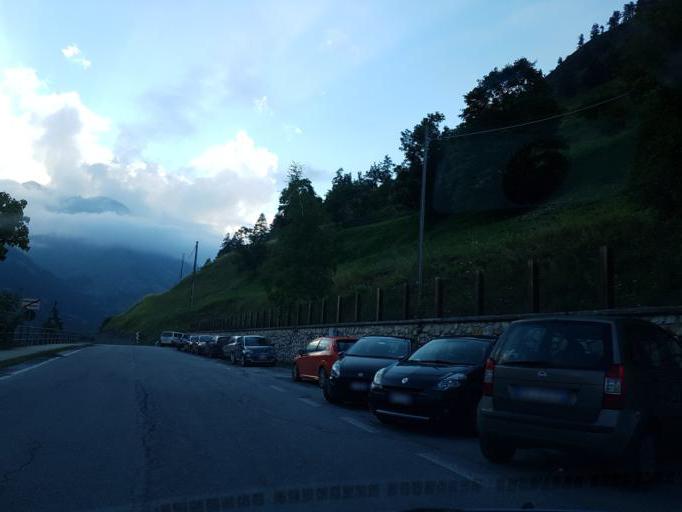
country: IT
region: Piedmont
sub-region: Provincia di Cuneo
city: Pontechianale
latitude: 44.6153
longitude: 7.0482
